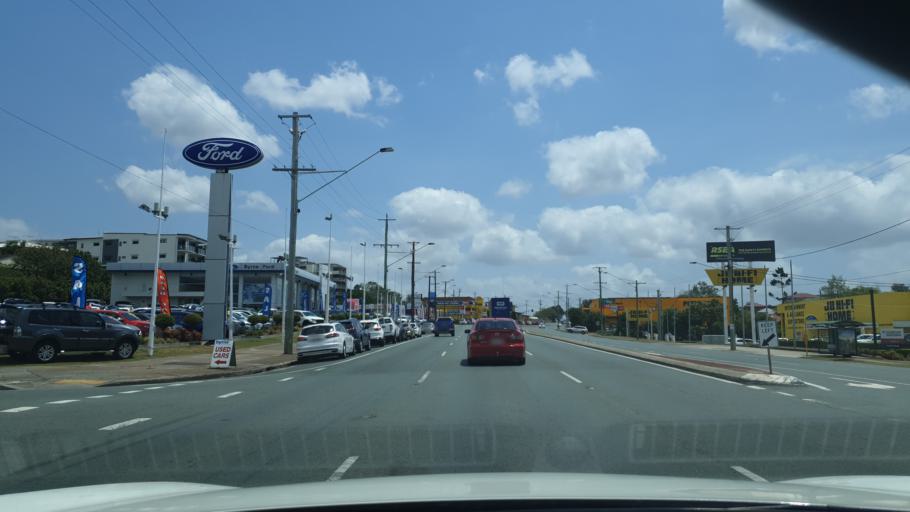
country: AU
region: Queensland
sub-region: Brisbane
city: Wavell Heights
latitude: -27.3966
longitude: 153.0310
